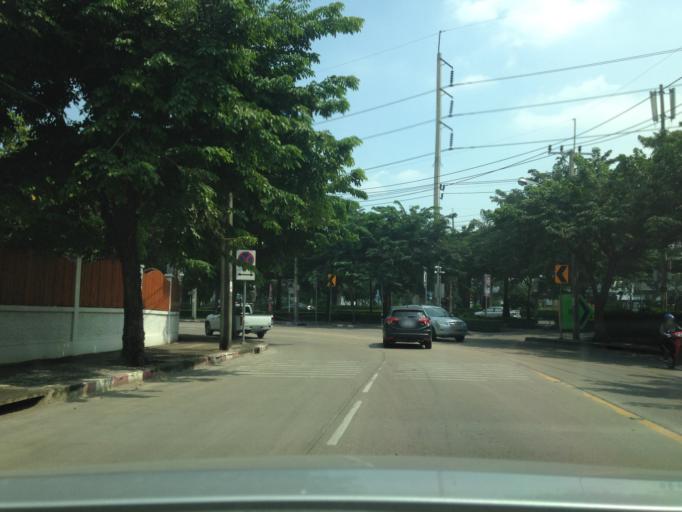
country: TH
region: Bangkok
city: Lat Phrao
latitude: 13.8357
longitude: 100.6312
